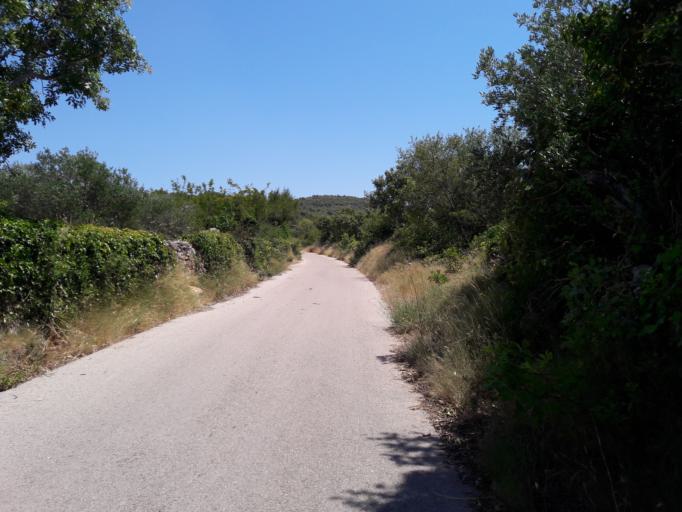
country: HR
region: Sibensko-Kniniska
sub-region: Grad Sibenik
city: Sibenik
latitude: 43.6913
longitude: 15.8502
